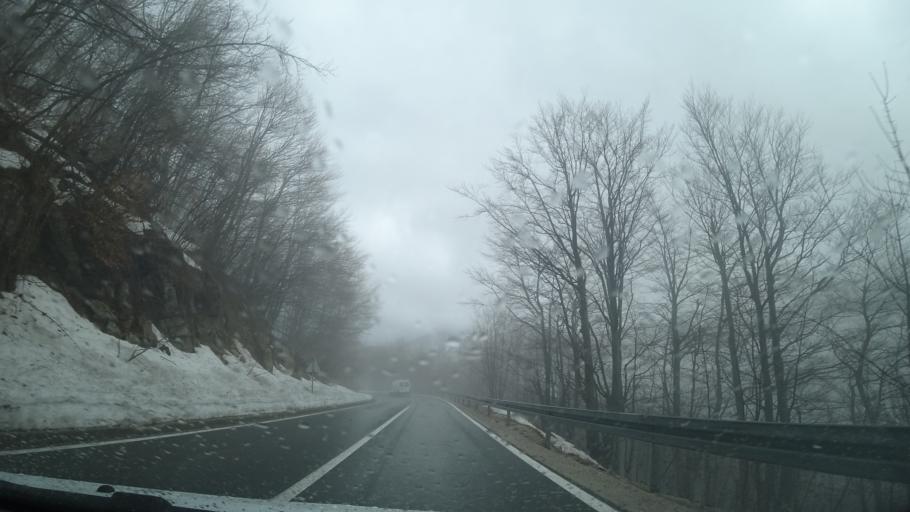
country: HR
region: Licko-Senjska
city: Popovaca
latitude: 44.5174
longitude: 15.1988
